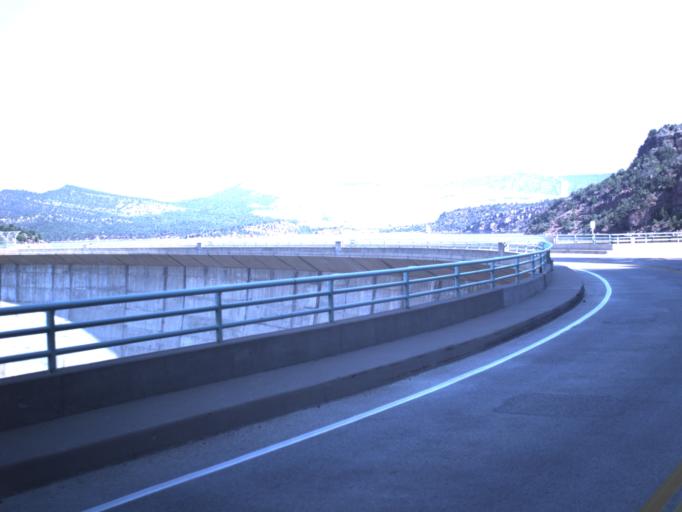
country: US
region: Utah
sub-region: Daggett County
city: Manila
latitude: 40.9144
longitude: -109.4197
